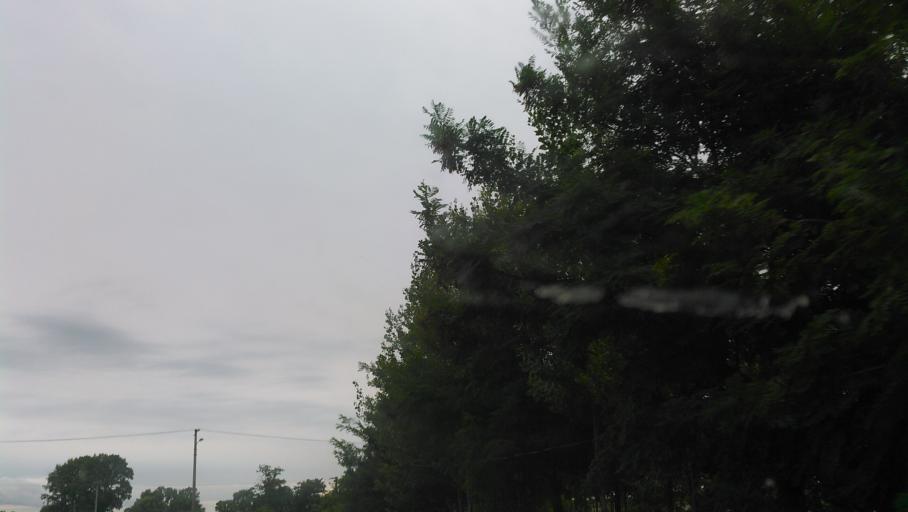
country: SK
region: Trnavsky
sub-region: Okres Dunajska Streda
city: Velky Meder
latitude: 47.9074
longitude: 17.8628
